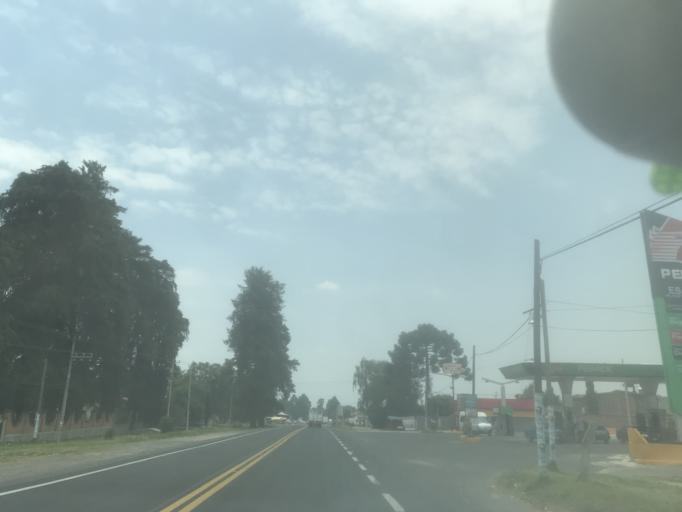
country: MX
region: Mexico
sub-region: Amecameca
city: San Diego Huehuecalco
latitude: 19.0870
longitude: -98.7820
